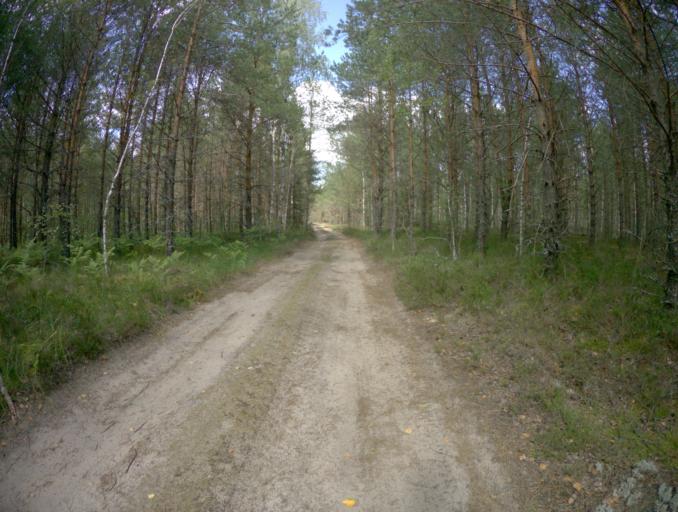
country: RU
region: Vladimir
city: Raduzhnyy
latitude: 55.9560
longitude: 40.2025
